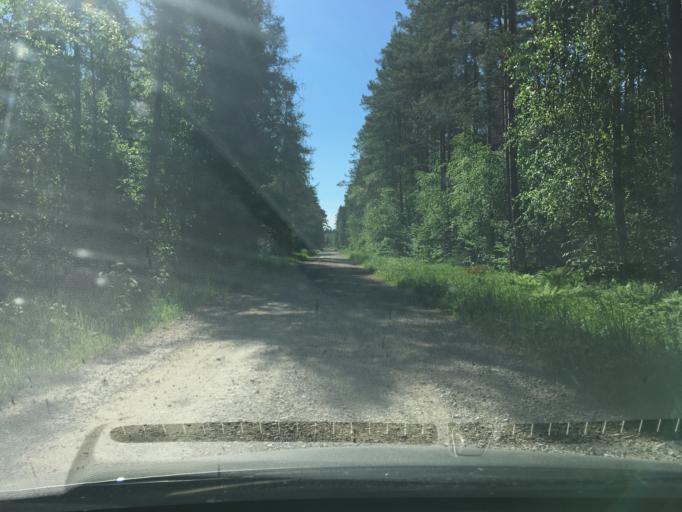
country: EE
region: Laeaene
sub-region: Lihula vald
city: Lihula
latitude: 58.6366
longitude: 23.7954
